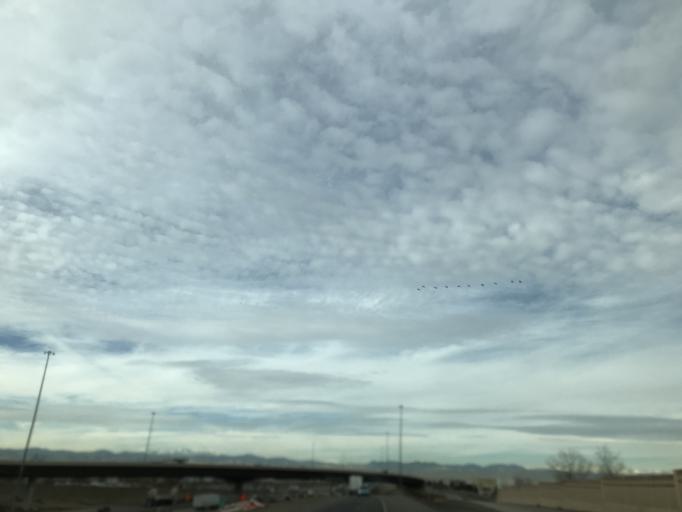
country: US
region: Colorado
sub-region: Adams County
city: Aurora
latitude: 39.7730
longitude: -104.8269
